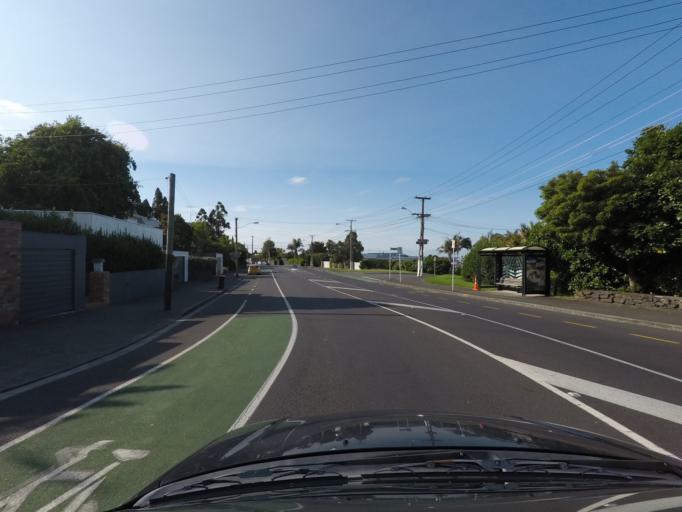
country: NZ
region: Auckland
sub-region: Auckland
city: Auckland
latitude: -36.8903
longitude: 174.7242
